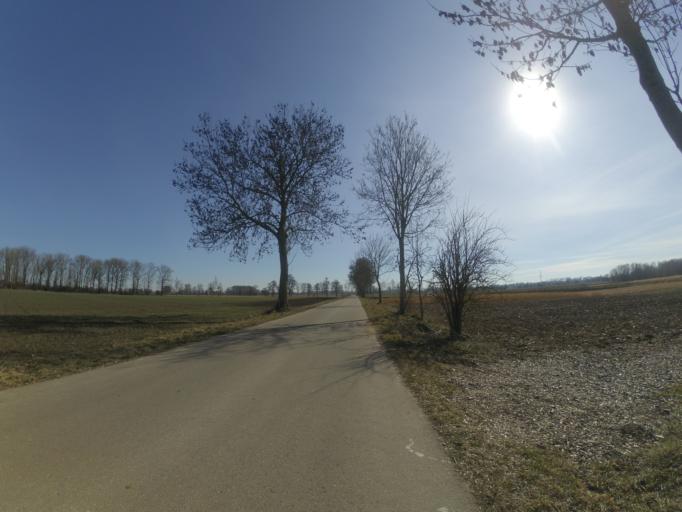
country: DE
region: Baden-Wuerttemberg
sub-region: Tuebingen Region
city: Rammingen
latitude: 48.4991
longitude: 10.1537
